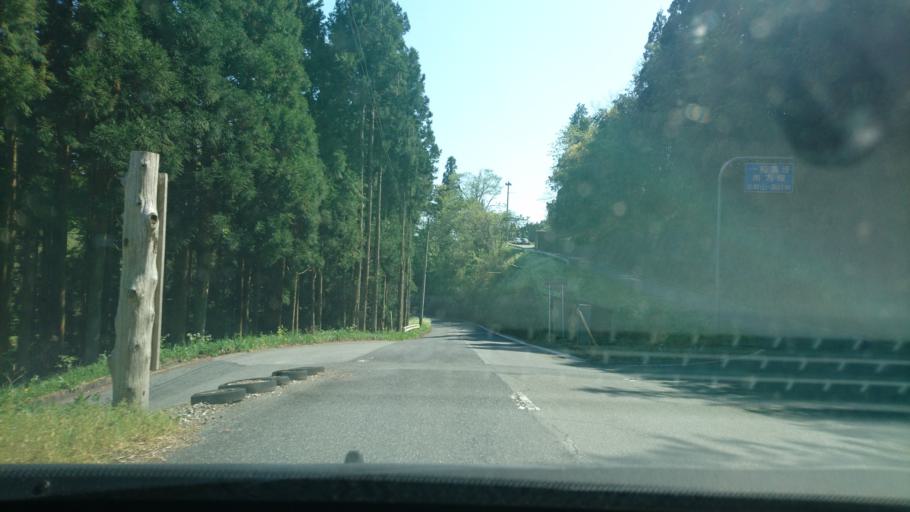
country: JP
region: Iwate
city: Ichinoseki
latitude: 38.9171
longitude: 141.2785
